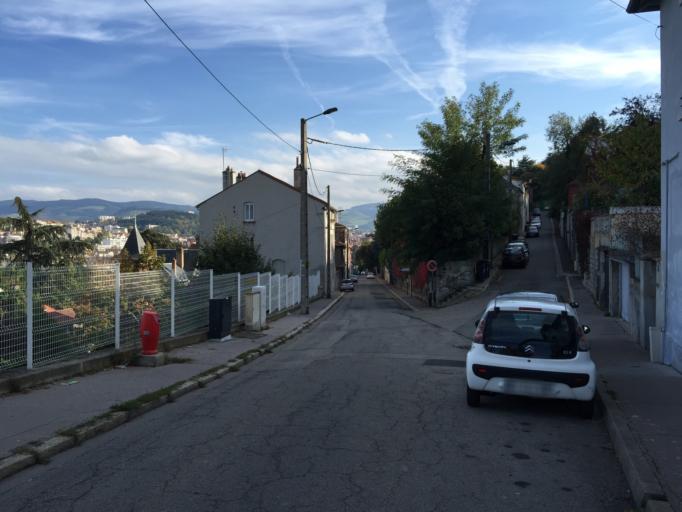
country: FR
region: Rhone-Alpes
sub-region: Departement de la Loire
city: Saint-Etienne
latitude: 45.4486
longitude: 4.3778
